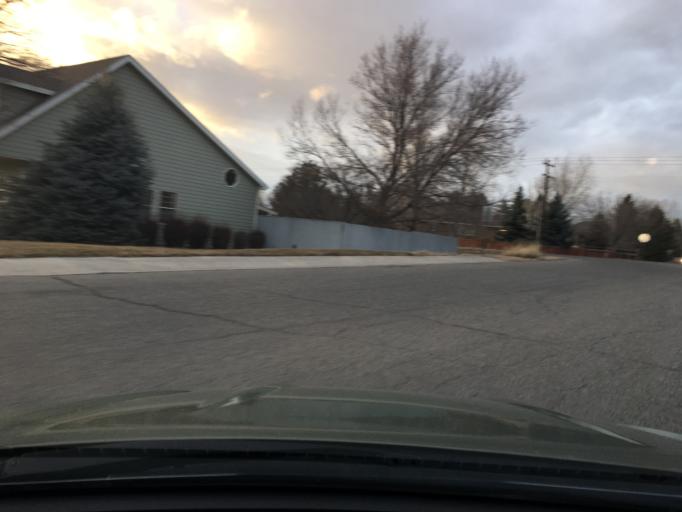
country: US
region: Colorado
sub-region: Montrose County
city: Montrose
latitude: 38.4668
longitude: -107.8406
